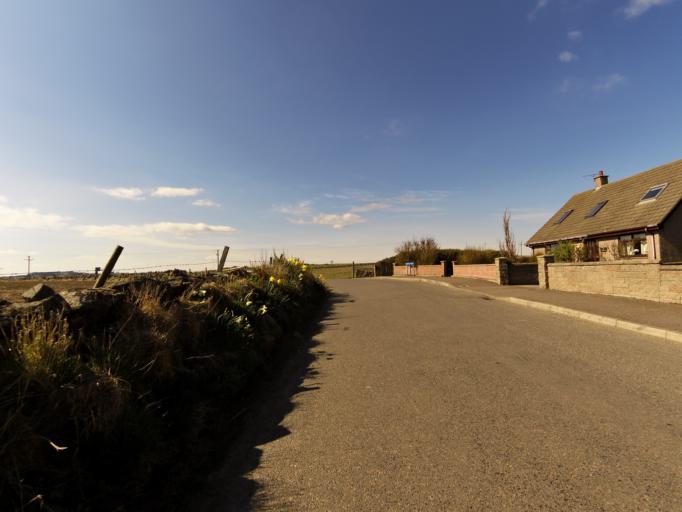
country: GB
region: Scotland
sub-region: Aberdeenshire
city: Portlethen
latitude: 57.0694
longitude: -2.1080
